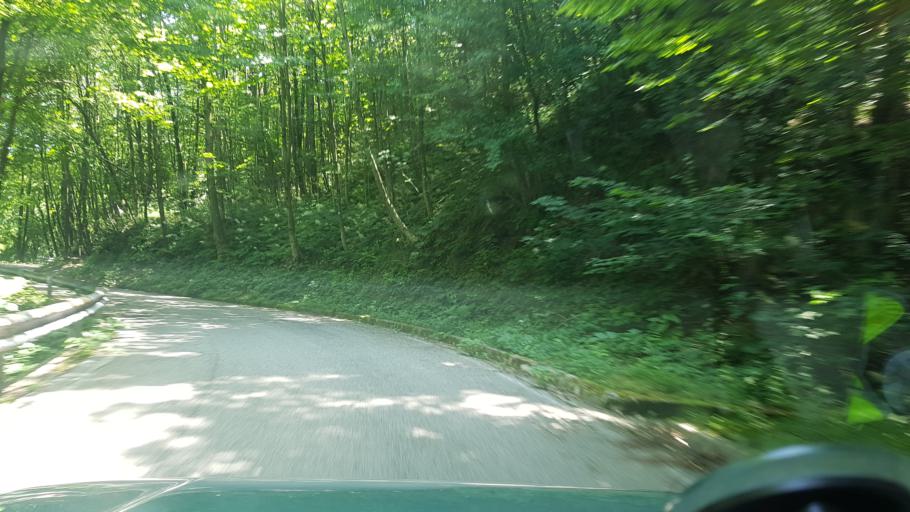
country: IT
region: Friuli Venezia Giulia
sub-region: Provincia di Udine
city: Lusevera
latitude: 46.2460
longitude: 13.2796
